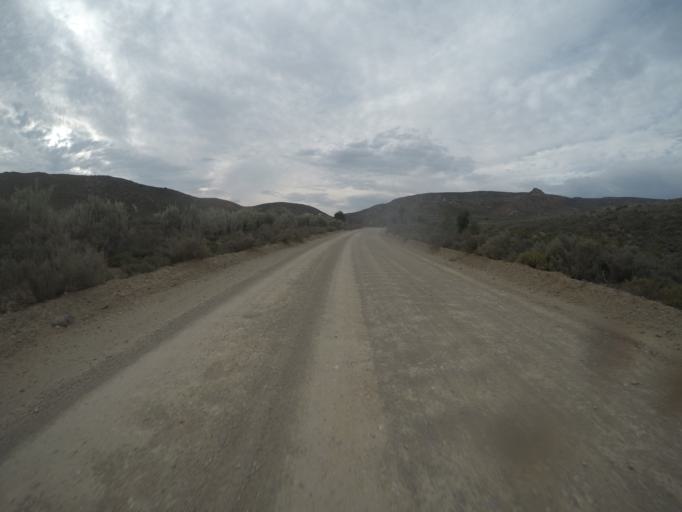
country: ZA
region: Eastern Cape
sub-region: Cacadu District Municipality
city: Willowmore
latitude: -33.5004
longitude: 23.6371
